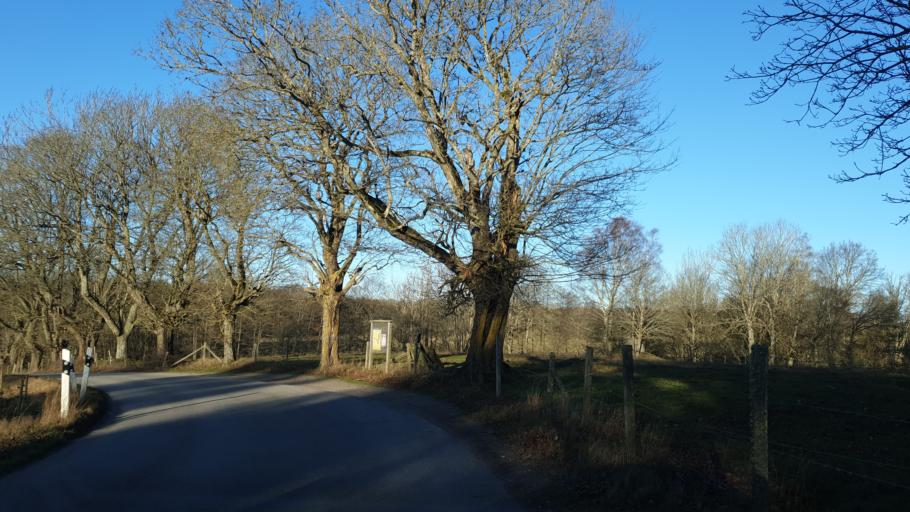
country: SE
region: Blekinge
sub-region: Karlskrona Kommun
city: Nattraby
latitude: 56.2442
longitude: 15.4222
